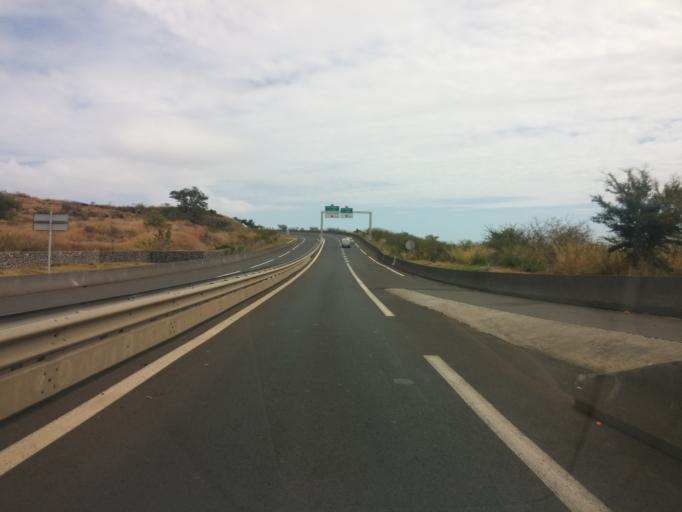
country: RE
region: Reunion
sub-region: Reunion
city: Saint-Paul
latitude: -21.0199
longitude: 55.2612
